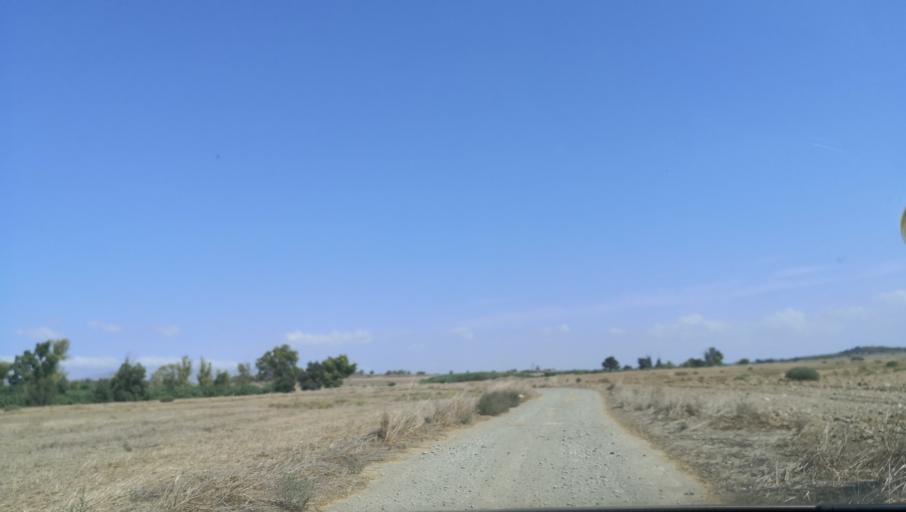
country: CY
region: Lefkosia
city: Mammari
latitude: 35.1781
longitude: 33.2251
